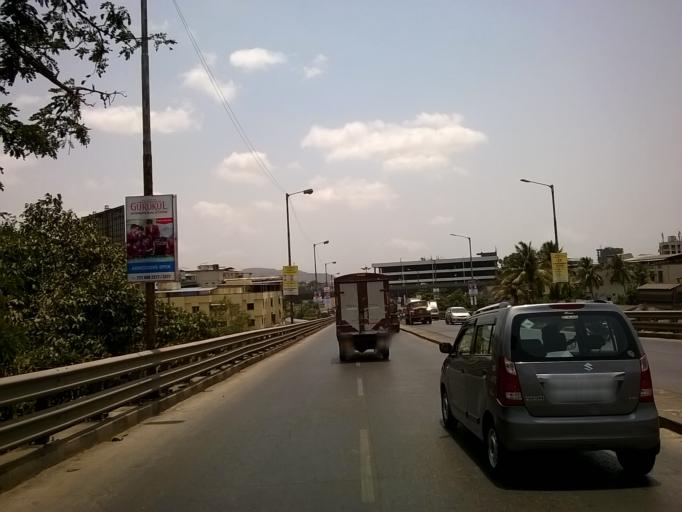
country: IN
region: Maharashtra
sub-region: Raigarh
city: Panvel
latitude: 18.9953
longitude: 73.1162
